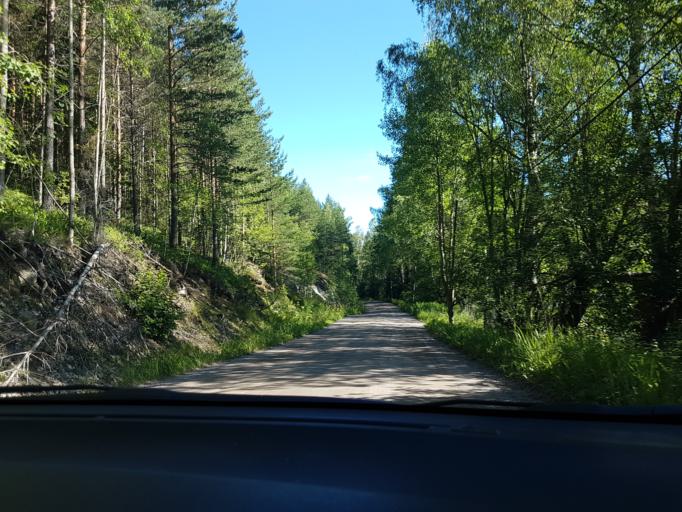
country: FI
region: Uusimaa
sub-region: Helsinki
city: Sibbo
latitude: 60.2749
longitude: 25.2347
